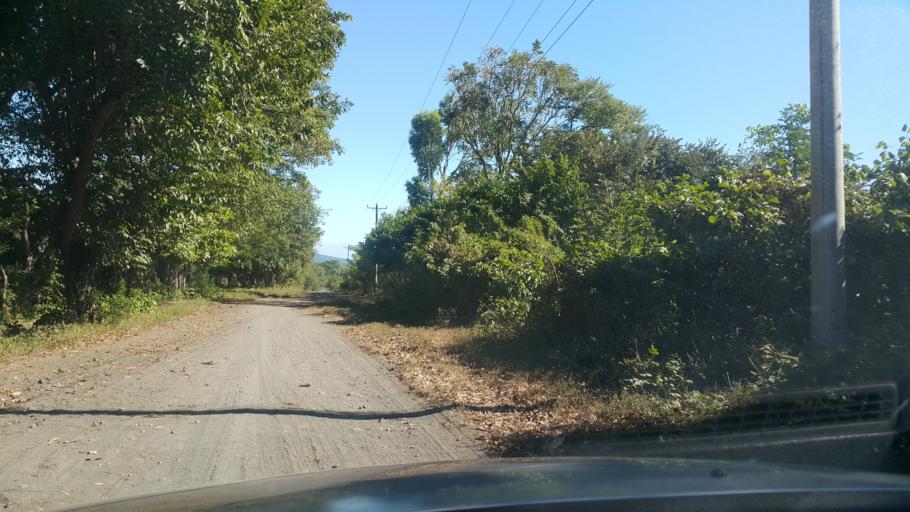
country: NI
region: Rivas
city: Altagracia
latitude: 11.4940
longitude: -85.6203
